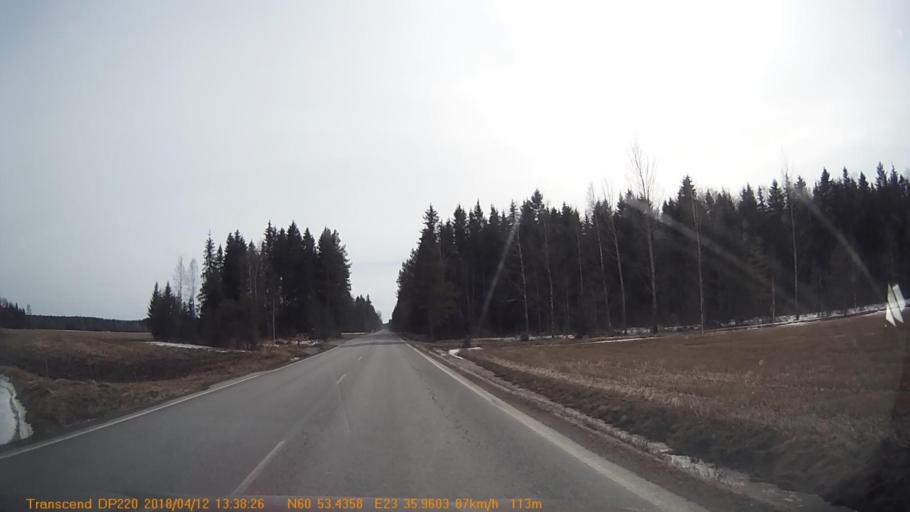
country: FI
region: Haeme
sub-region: Forssa
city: Forssa
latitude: 60.8904
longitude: 23.5994
